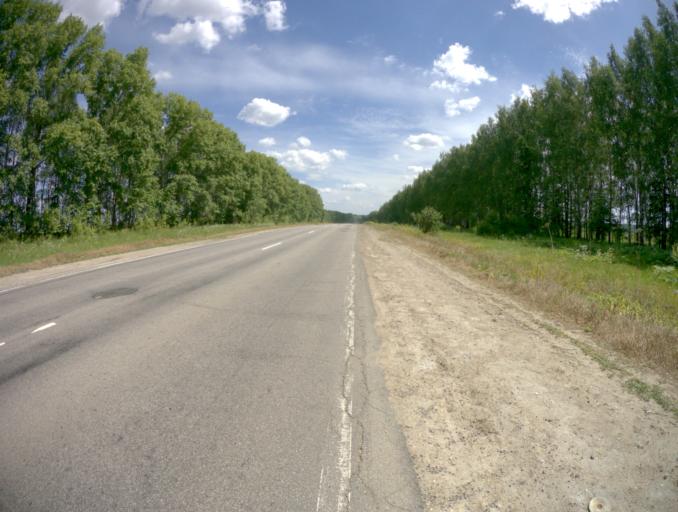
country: RU
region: Ivanovo
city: Gavrilov Posad
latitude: 56.3790
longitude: 40.0137
